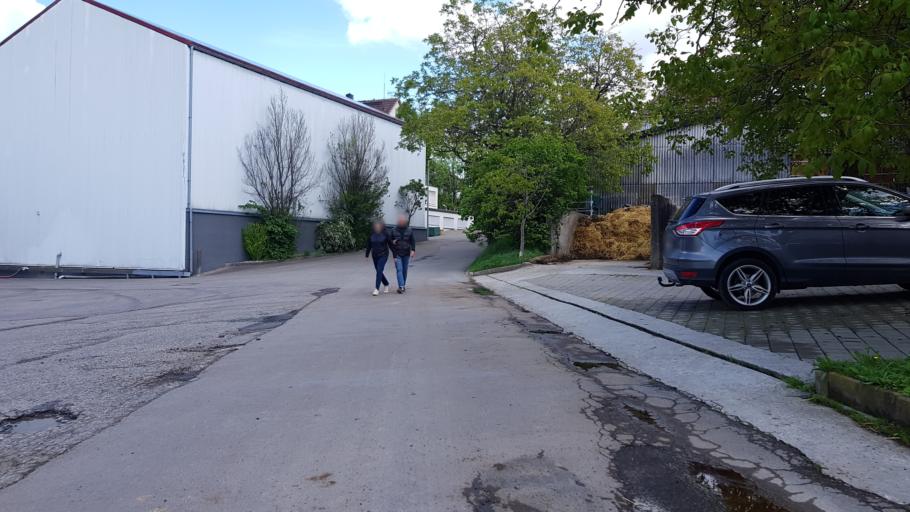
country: DE
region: Baden-Wuerttemberg
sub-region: Regierungsbezirk Stuttgart
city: Affalterbach
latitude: 48.9355
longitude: 9.3217
